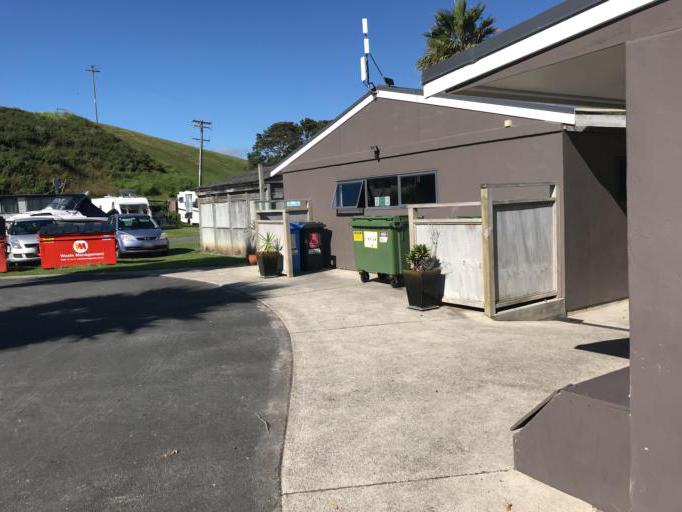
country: NZ
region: Bay of Plenty
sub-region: Western Bay of Plenty District
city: Waihi Beach
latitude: -37.4640
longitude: 175.9870
